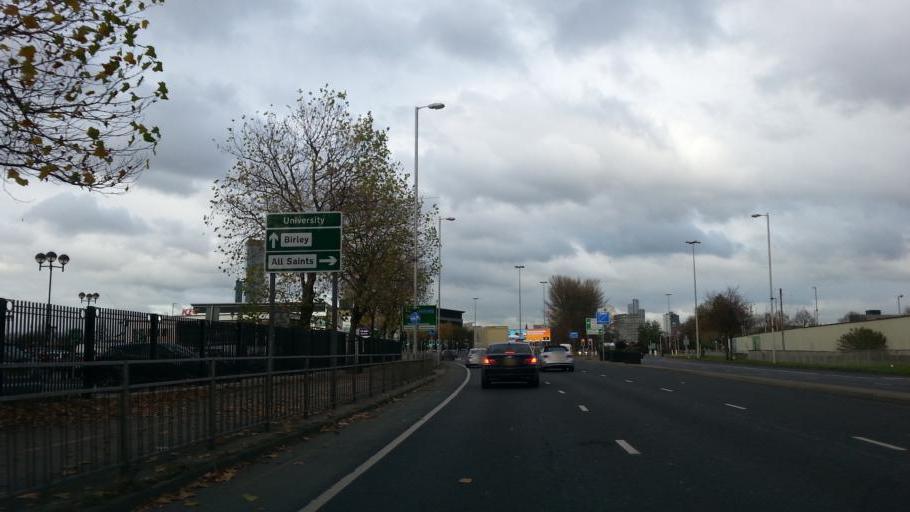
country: GB
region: England
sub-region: Manchester
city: Hulme
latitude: 53.4611
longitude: -2.2451
